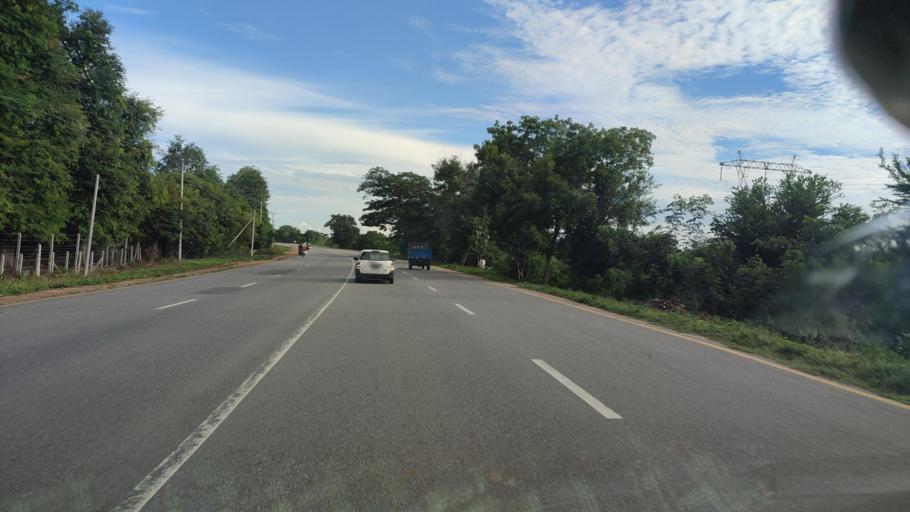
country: MM
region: Mandalay
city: Yamethin
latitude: 20.2044
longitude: 96.1805
